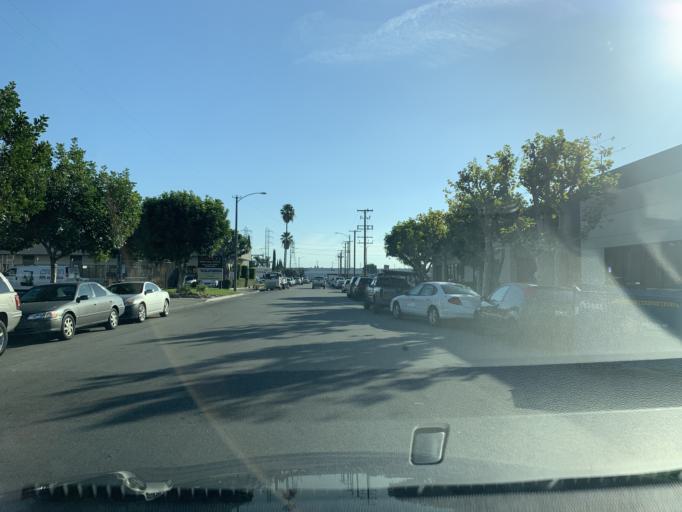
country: US
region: California
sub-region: Orange County
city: Anaheim
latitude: 33.8130
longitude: -117.9001
